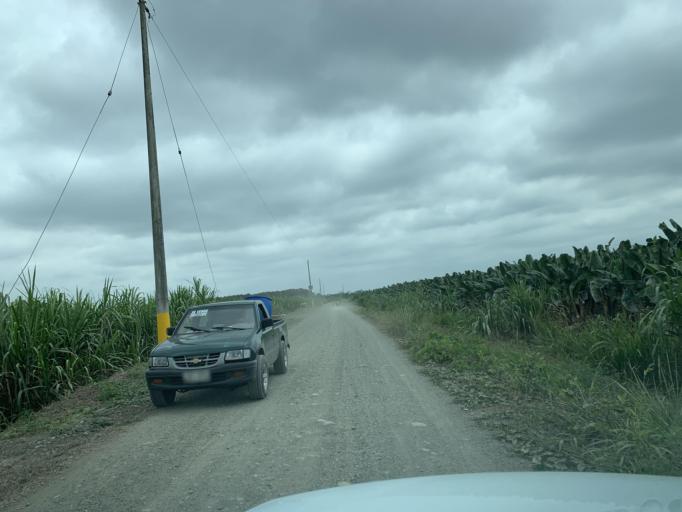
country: EC
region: Guayas
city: Coronel Marcelino Mariduena
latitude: -2.3355
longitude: -79.4557
